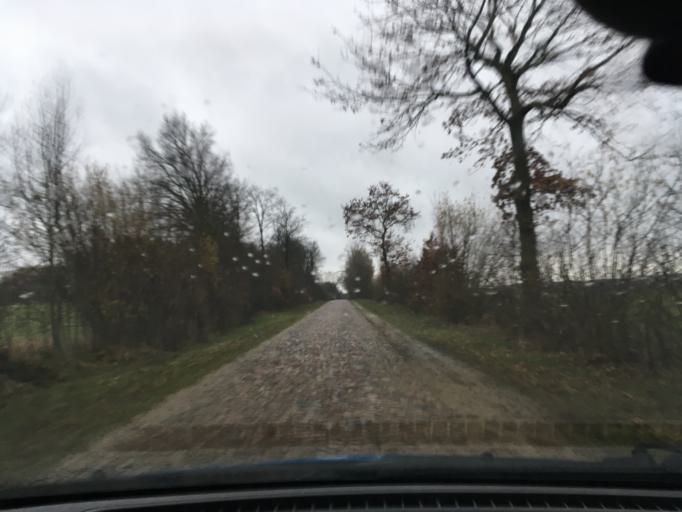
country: DE
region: Schleswig-Holstein
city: Kruzen
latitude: 53.4126
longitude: 10.5257
